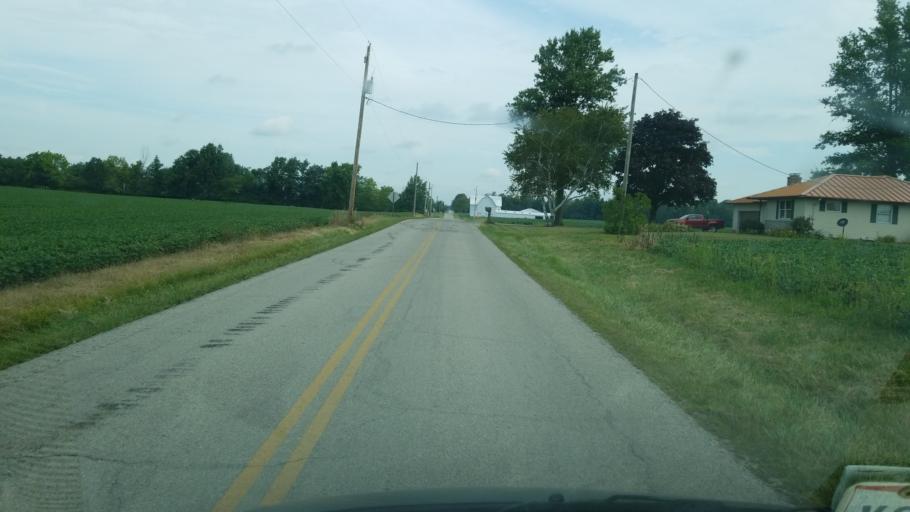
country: US
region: Ohio
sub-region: Seneca County
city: Tiffin
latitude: 41.0822
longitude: -83.0931
